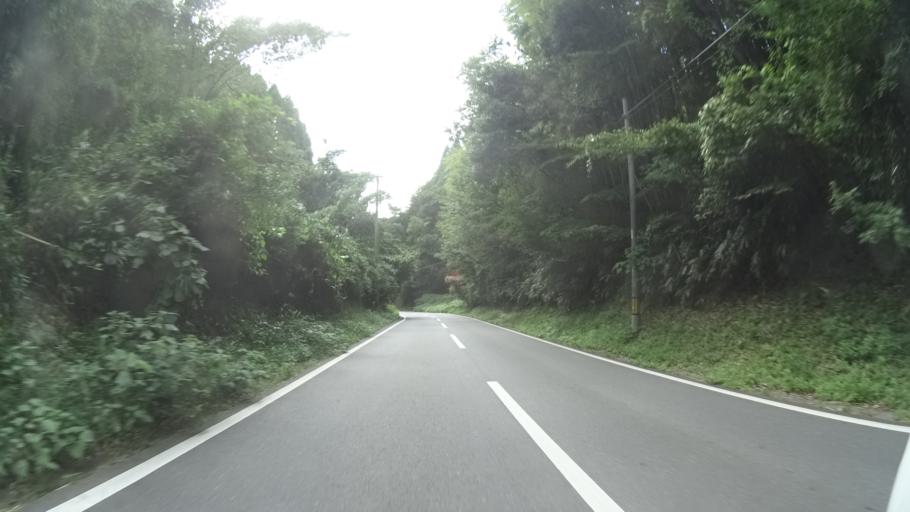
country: JP
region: Kumamoto
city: Aso
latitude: 32.7097
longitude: 131.1350
